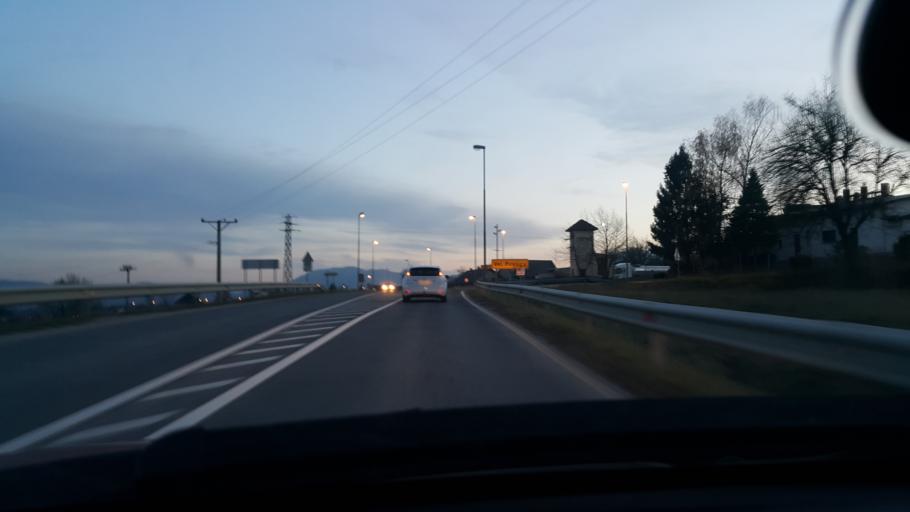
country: SI
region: Zalec
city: Gotovlje
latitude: 46.2873
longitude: 15.1759
